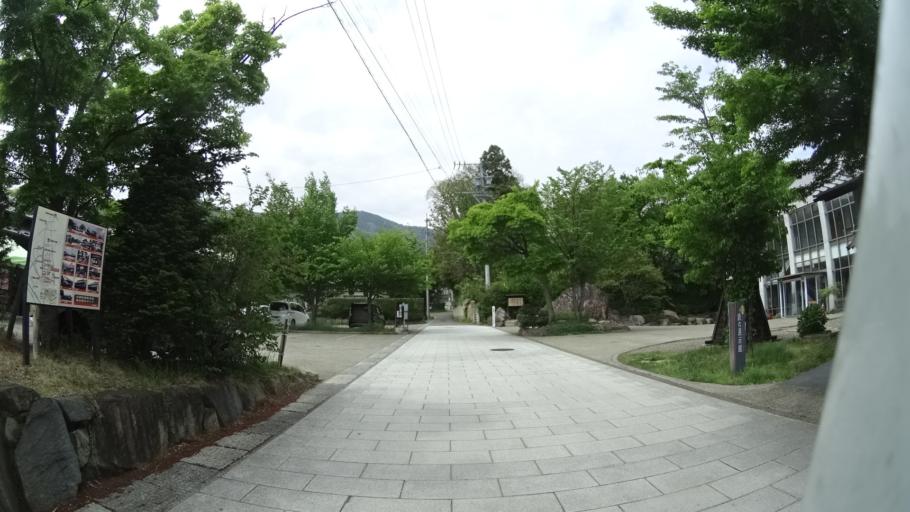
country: JP
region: Nagano
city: Ueda
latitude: 36.4634
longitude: 138.1827
